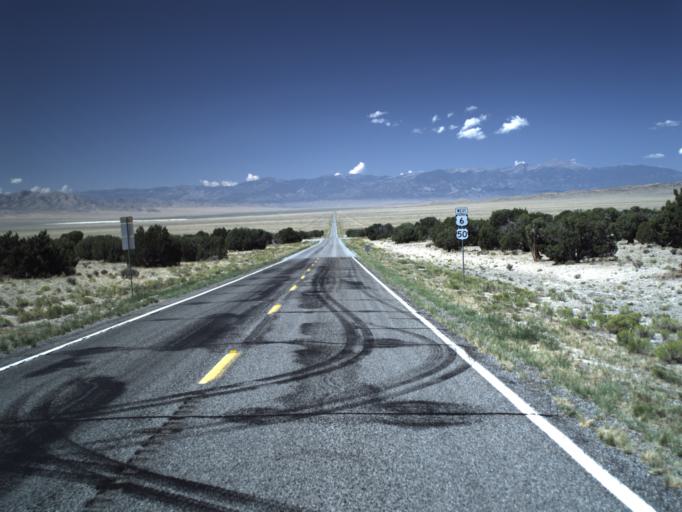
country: US
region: Utah
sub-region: Beaver County
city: Milford
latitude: 39.0754
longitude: -113.7138
